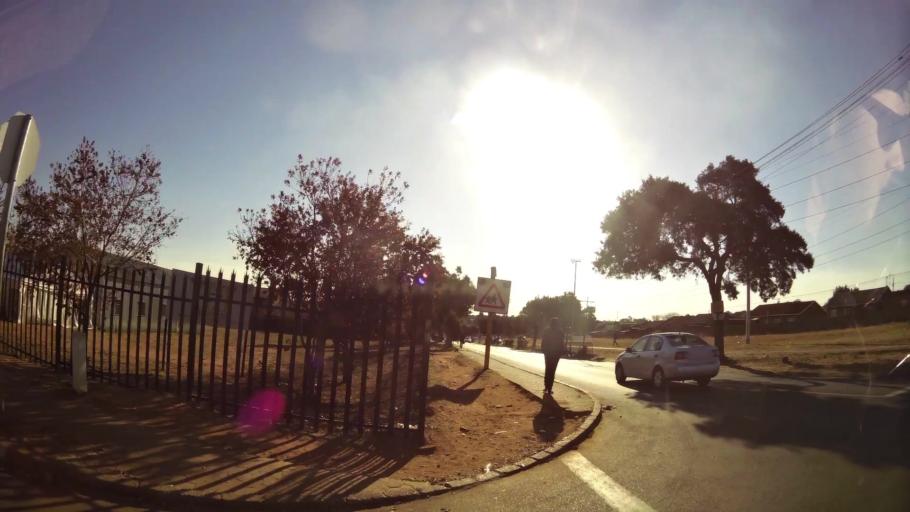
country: ZA
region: Gauteng
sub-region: City of Johannesburg Metropolitan Municipality
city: Johannesburg
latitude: -26.2132
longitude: 27.9780
